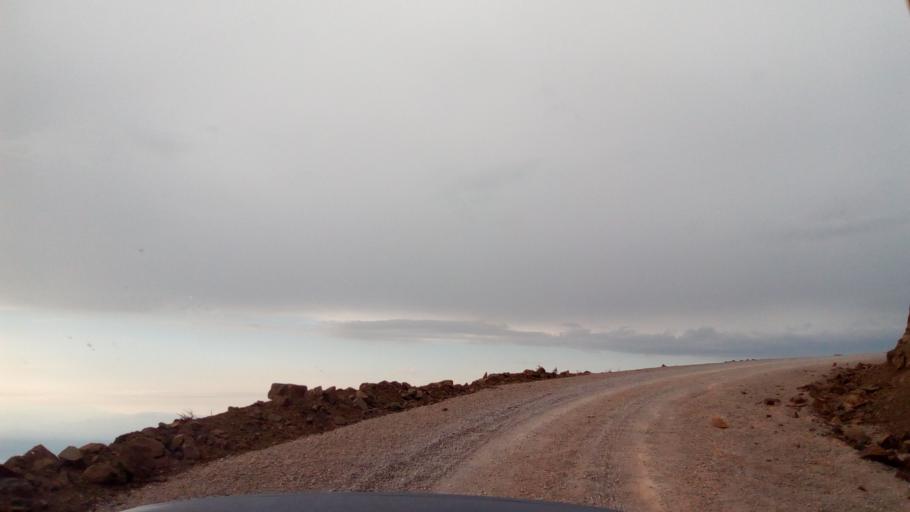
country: GR
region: Central Greece
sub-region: Nomos Fokidos
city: Lidoriki
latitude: 38.4555
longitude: 22.0788
